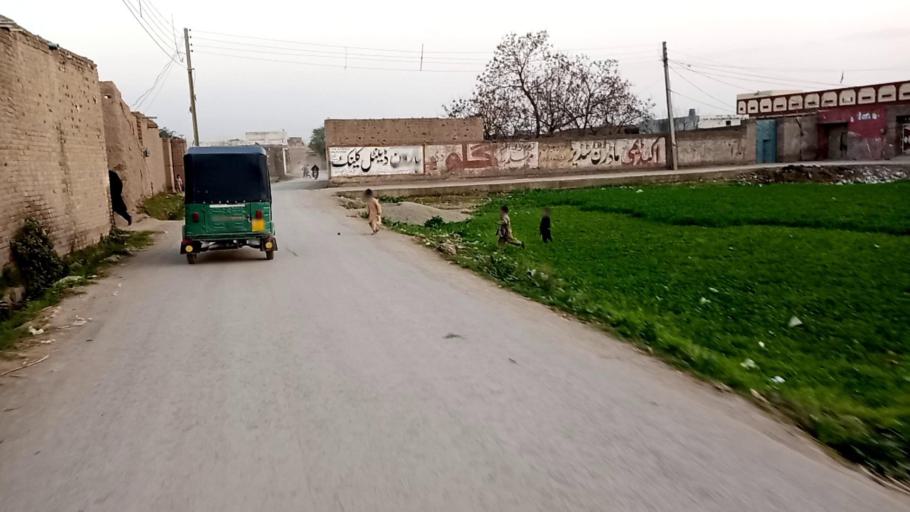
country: PK
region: Khyber Pakhtunkhwa
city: Peshawar
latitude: 34.0308
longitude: 71.4946
